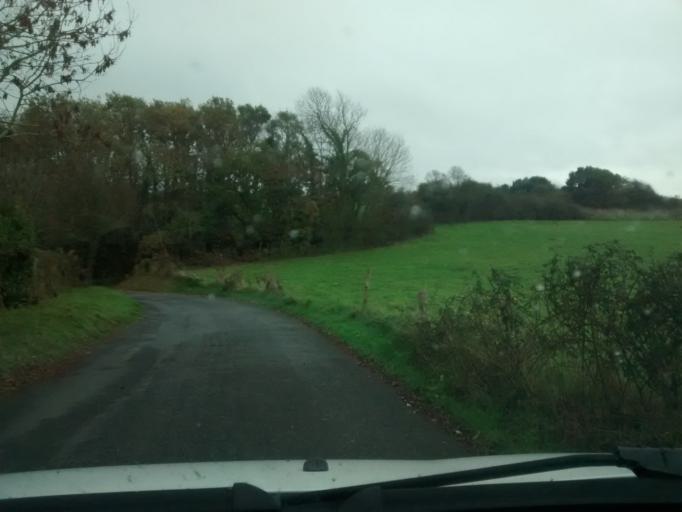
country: FR
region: Lower Normandy
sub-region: Departement de la Manche
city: Jullouville
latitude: 48.7420
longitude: -1.5628
